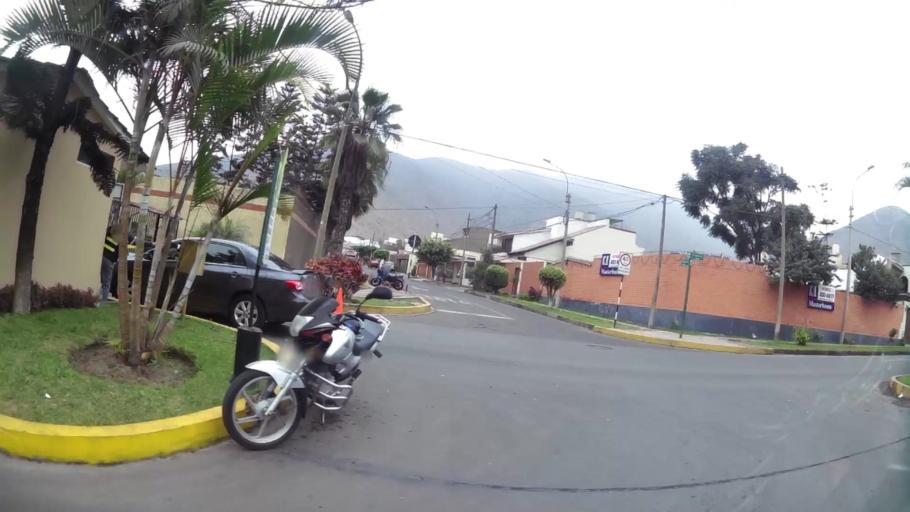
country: PE
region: Lima
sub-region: Lima
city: La Molina
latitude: -12.0931
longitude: -76.9262
